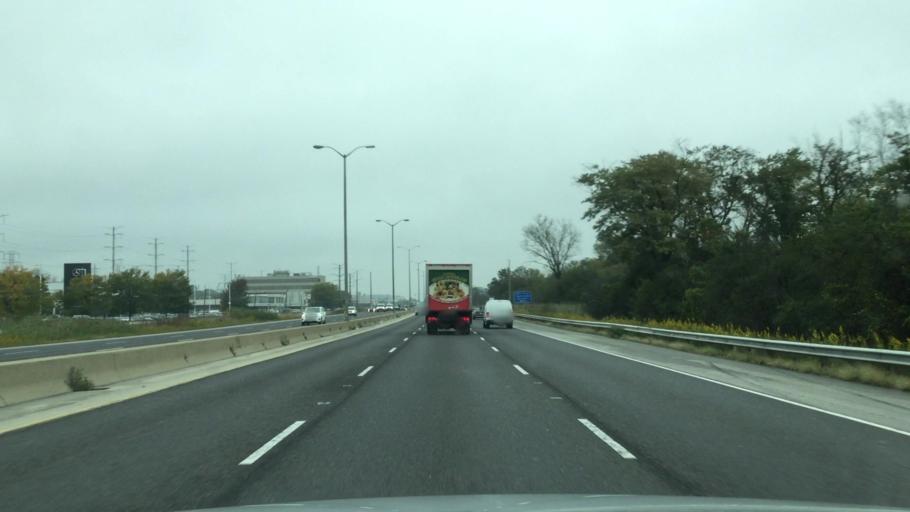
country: US
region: Illinois
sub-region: Cook County
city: Northfield
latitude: 42.1212
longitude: -87.7806
